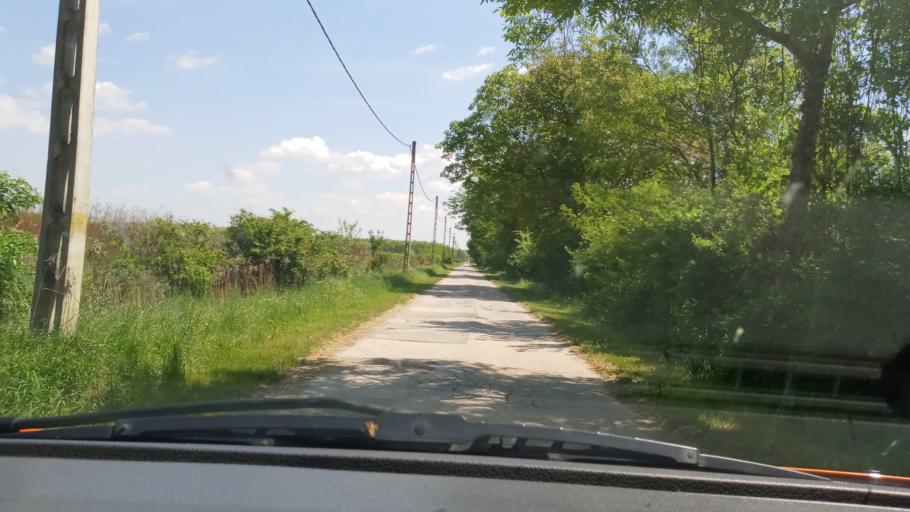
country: HU
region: Baranya
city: Siklos
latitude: 45.7708
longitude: 18.2778
